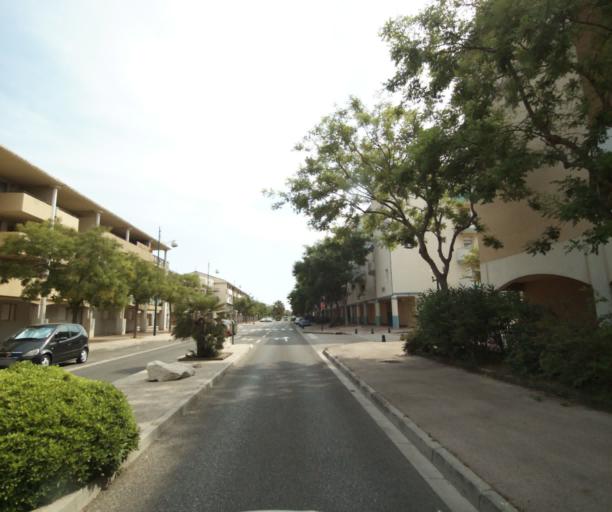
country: FR
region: Provence-Alpes-Cote d'Azur
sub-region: Departement du Var
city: La Garde
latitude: 43.1334
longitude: 6.0216
